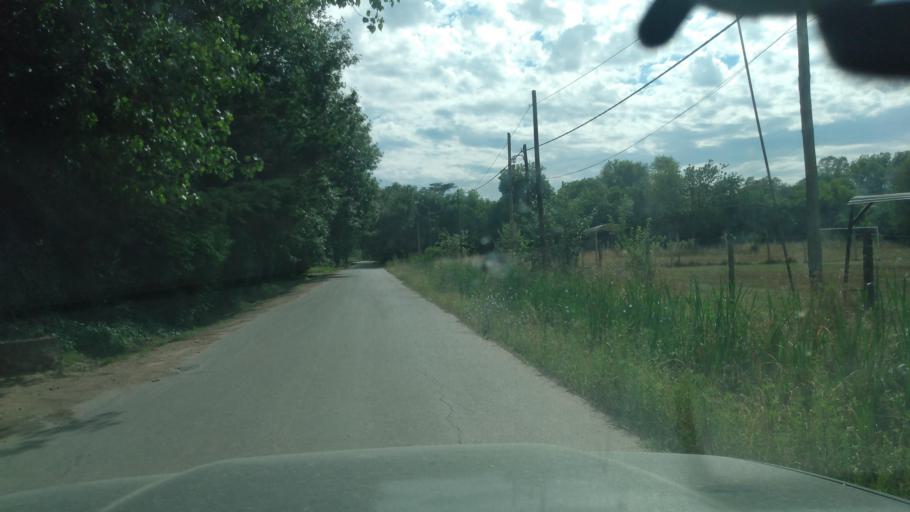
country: AR
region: Buenos Aires
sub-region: Partido de Lujan
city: Lujan
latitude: -34.5901
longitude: -59.0530
